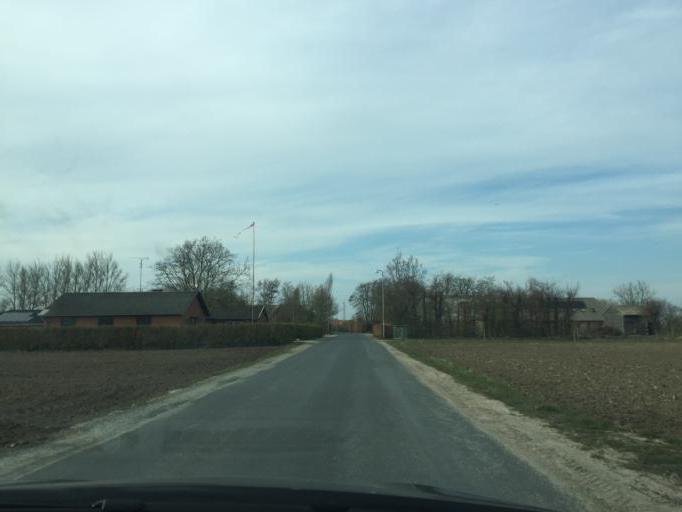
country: DK
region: South Denmark
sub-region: Faaborg-Midtfyn Kommune
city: Arslev
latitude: 55.3246
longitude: 10.5175
